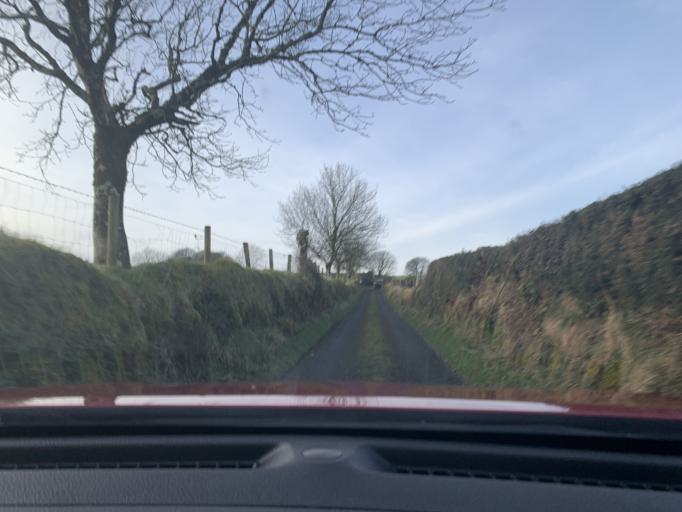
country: IE
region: Connaught
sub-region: Sligo
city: Strandhill
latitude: 54.1721
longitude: -8.6586
